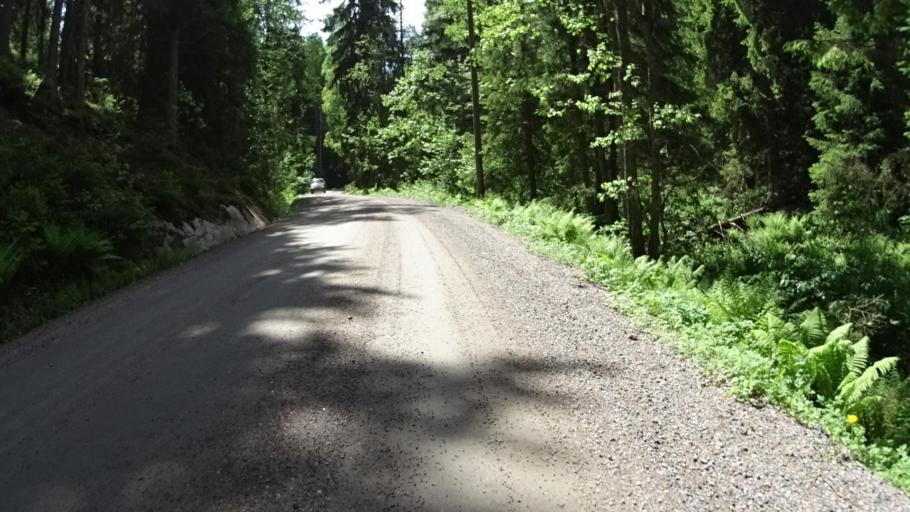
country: FI
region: Uusimaa
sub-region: Helsinki
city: Kauniainen
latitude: 60.3096
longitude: 24.6843
